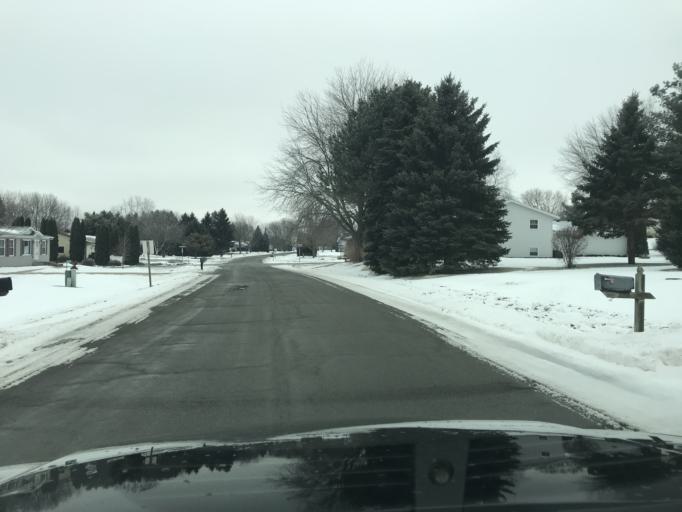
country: US
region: Wisconsin
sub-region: Dane County
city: Cottage Grove
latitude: 43.0967
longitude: -89.2163
